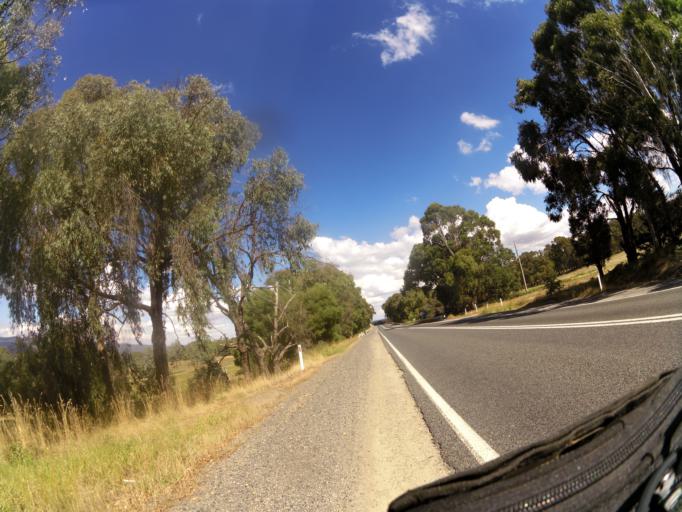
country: AU
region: Victoria
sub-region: Mansfield
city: Mansfield
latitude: -36.8872
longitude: 145.9952
